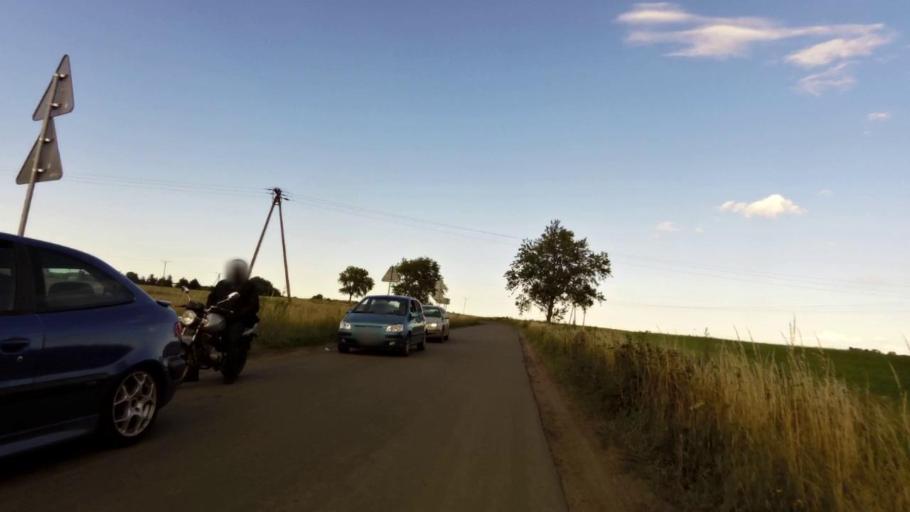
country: PL
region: West Pomeranian Voivodeship
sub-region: Powiat slawienski
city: Darlowo
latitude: 54.4036
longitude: 16.3812
